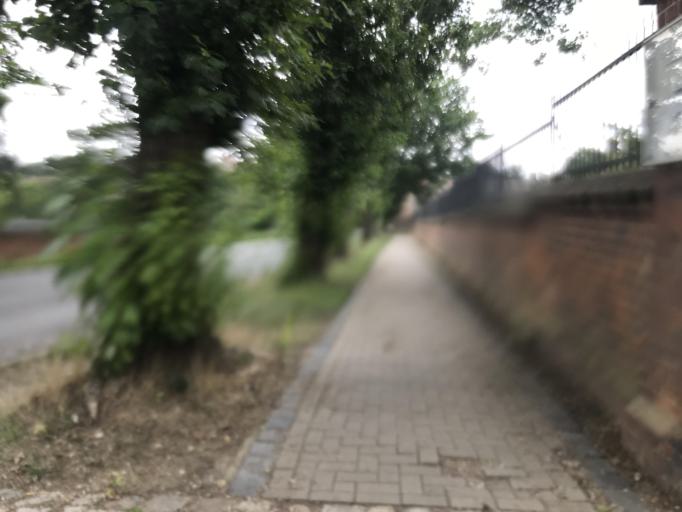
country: DE
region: Saxony-Anhalt
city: Quedlinburg
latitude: 51.7851
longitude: 11.1293
